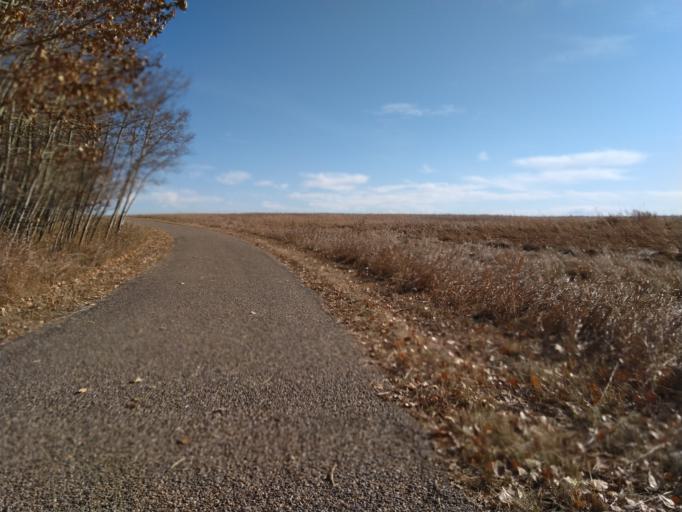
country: CA
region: Alberta
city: Calgary
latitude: 51.1236
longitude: -114.1282
